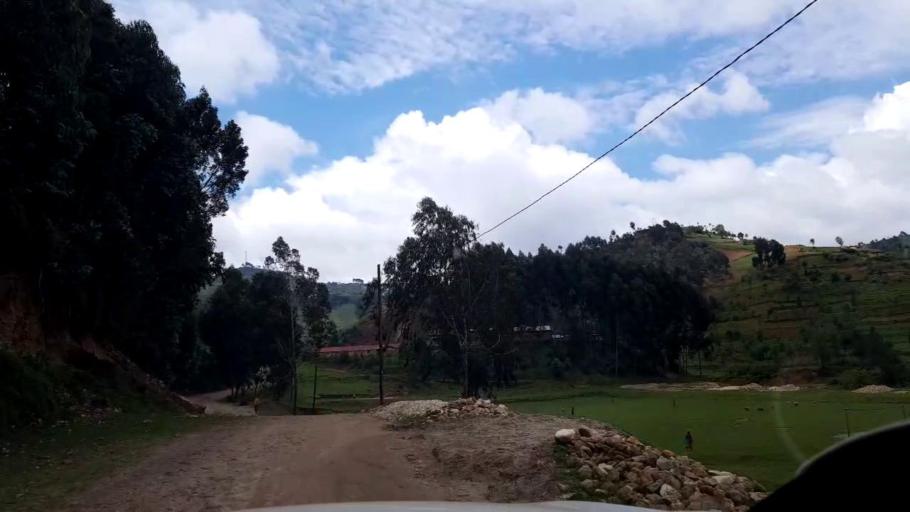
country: RW
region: Western Province
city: Kibuye
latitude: -1.9075
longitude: 29.4563
